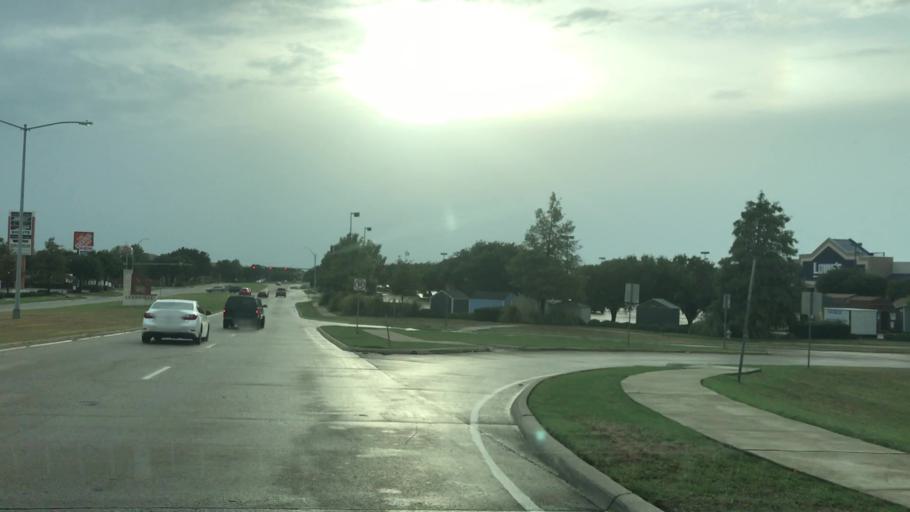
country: US
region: Texas
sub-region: Denton County
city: Lewisville
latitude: 33.0561
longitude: -97.0132
